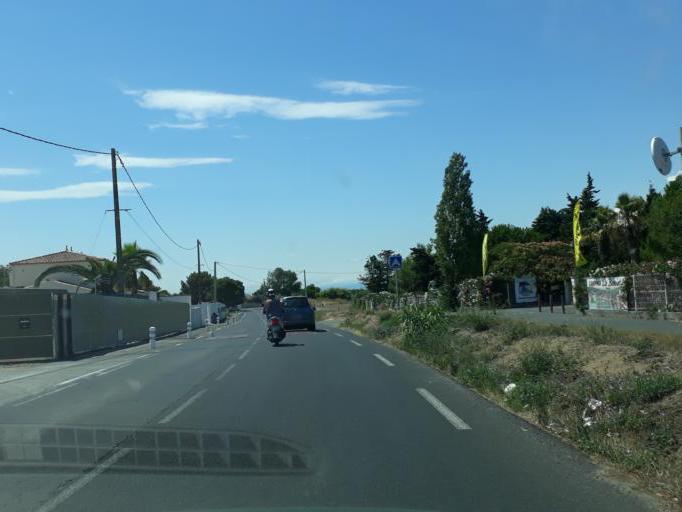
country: FR
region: Languedoc-Roussillon
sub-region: Departement de l'Herault
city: Agde
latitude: 43.2881
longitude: 3.4738
